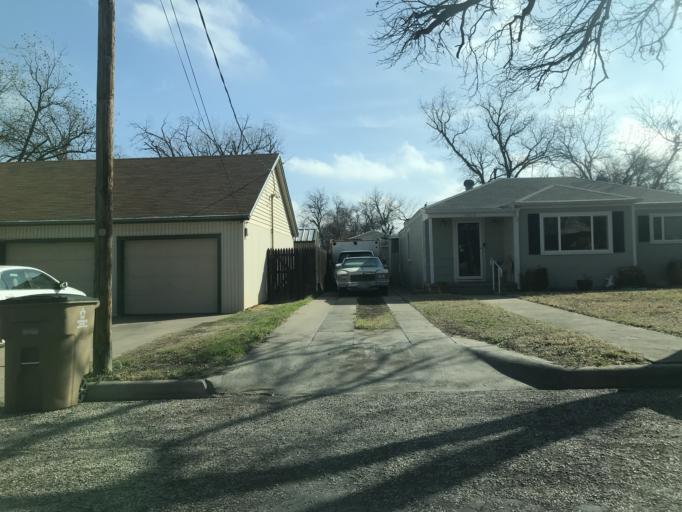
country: US
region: Texas
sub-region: Tom Green County
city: San Angelo
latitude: 31.4471
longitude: -100.4597
